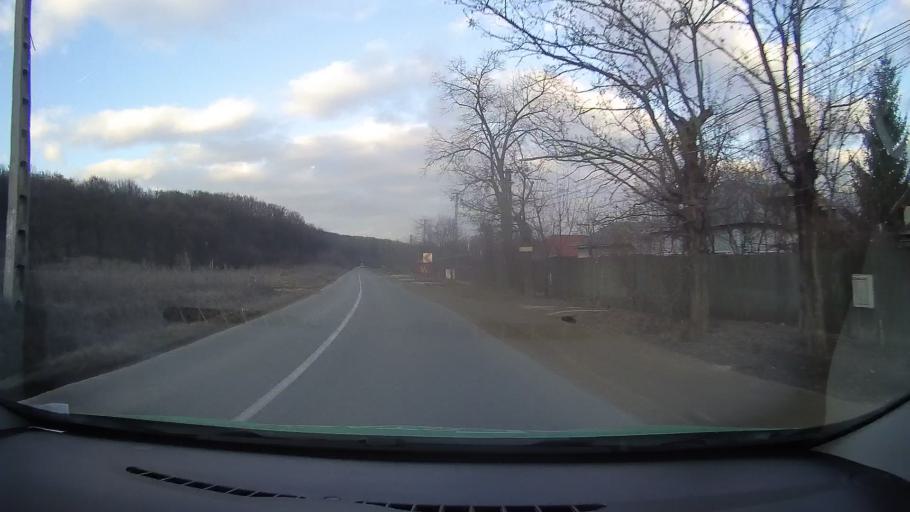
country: RO
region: Dambovita
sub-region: Comuna Gura Ocnitei
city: Gura Ocnitei
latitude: 44.9424
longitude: 25.5826
